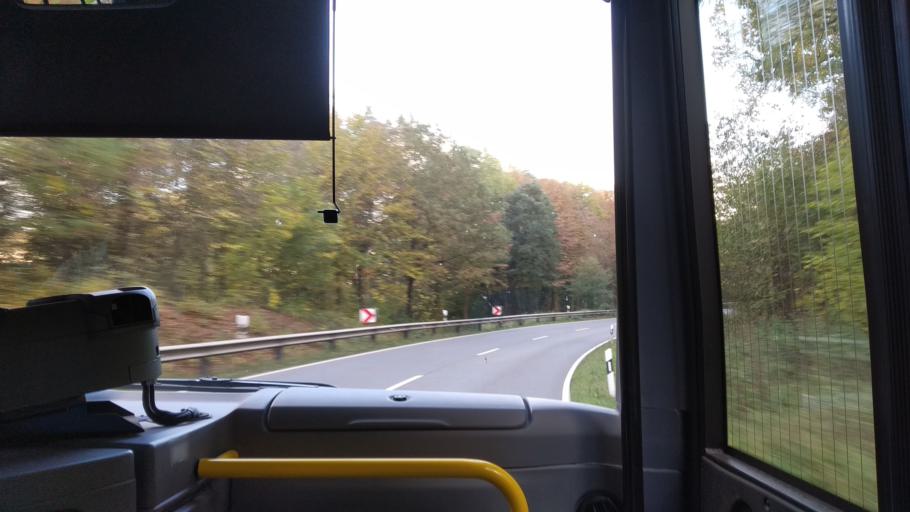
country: DE
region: Rheinland-Pfalz
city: Diez
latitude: 50.3651
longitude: 8.0263
